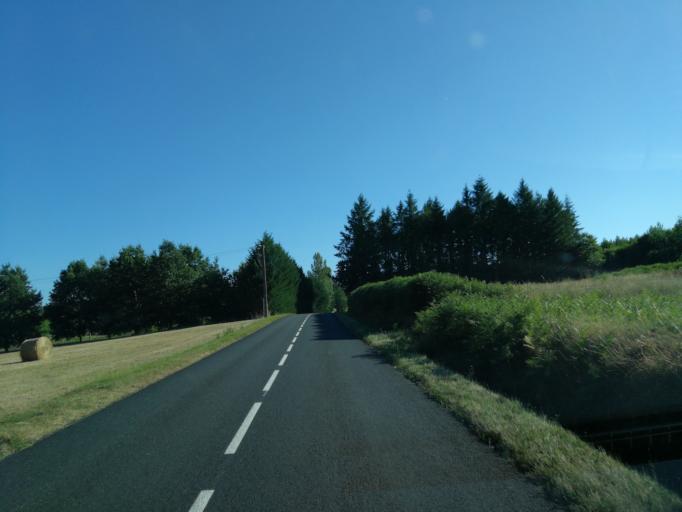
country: FR
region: Midi-Pyrenees
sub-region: Departement du Lot
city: Salviac
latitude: 44.6272
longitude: 1.2185
